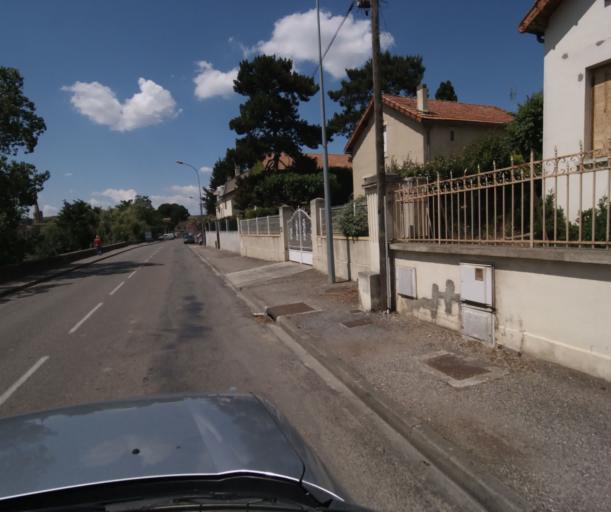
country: FR
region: Languedoc-Roussillon
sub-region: Departement de l'Aude
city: Limoux
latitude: 43.0501
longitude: 2.2228
